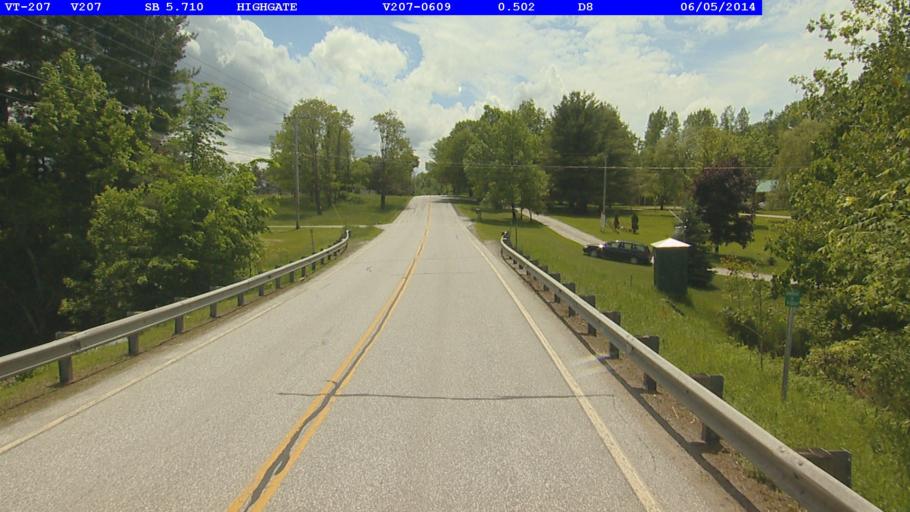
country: US
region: Vermont
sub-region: Franklin County
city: Swanton
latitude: 44.9186
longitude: -73.0555
